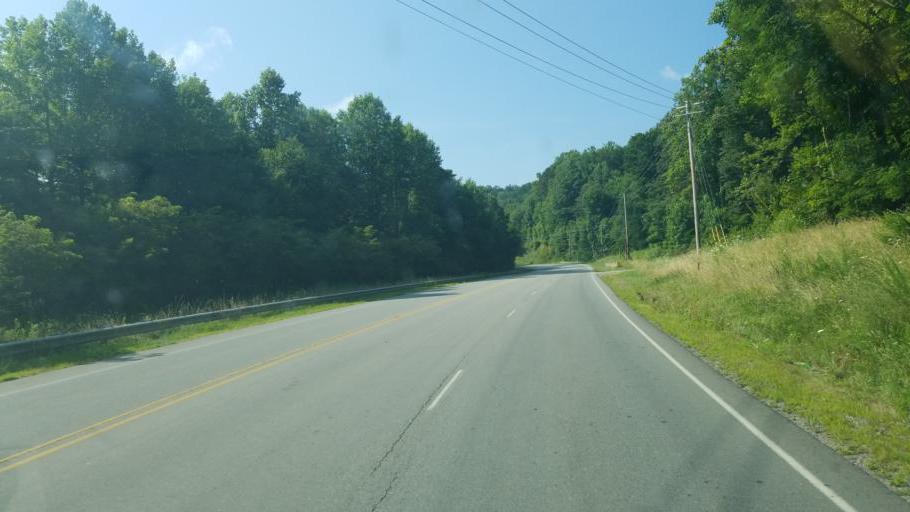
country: US
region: North Carolina
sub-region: Avery County
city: Newland
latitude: 36.1455
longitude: -81.9506
